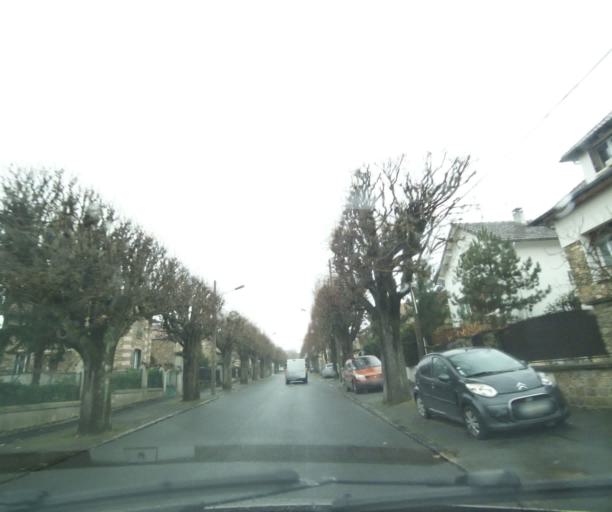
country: FR
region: Ile-de-France
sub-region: Departement du Val-de-Marne
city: Ablon-sur-Seine
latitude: 48.7325
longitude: 2.4167
